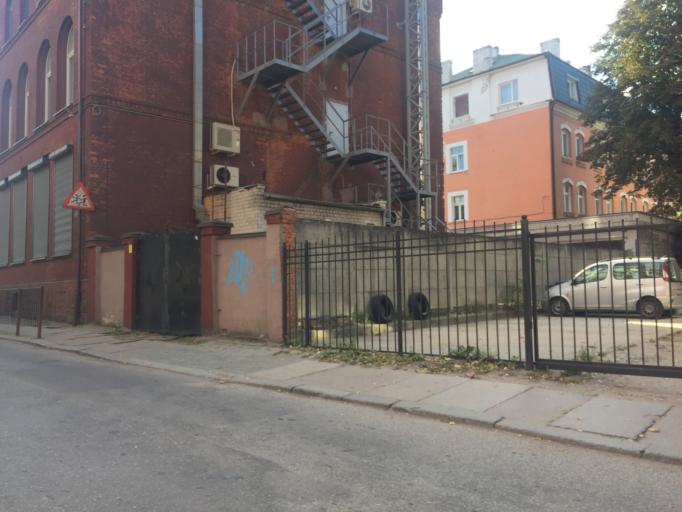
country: RU
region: Kaliningrad
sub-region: Gorod Kaliningrad
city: Kaliningrad
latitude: 54.6990
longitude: 20.5088
